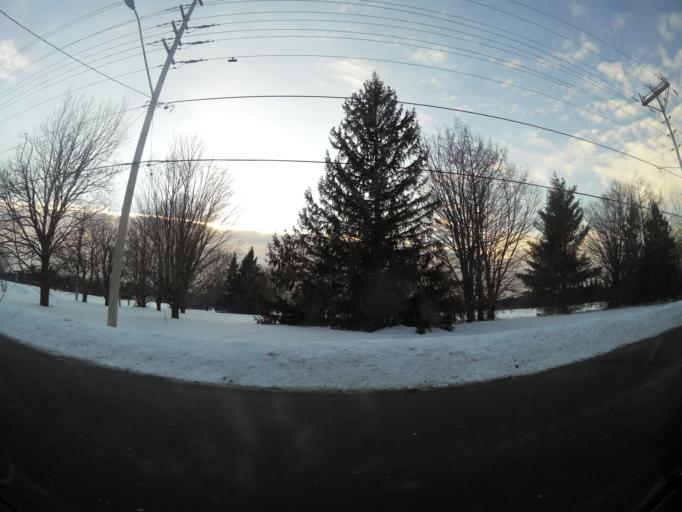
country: CA
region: Ontario
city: Ottawa
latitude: 45.4288
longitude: -75.5731
